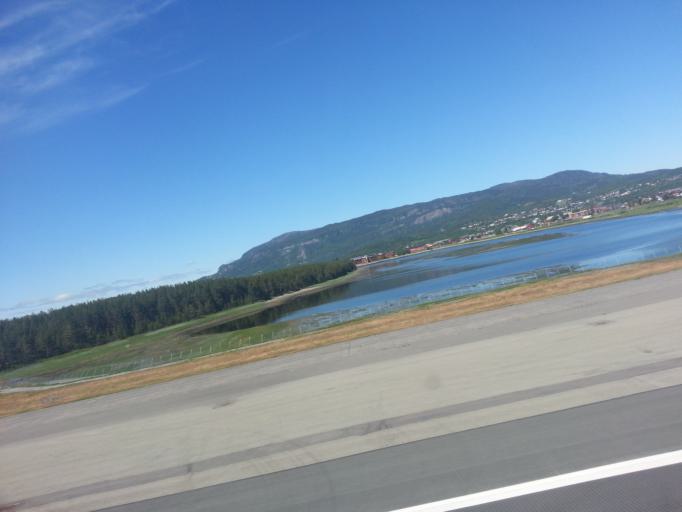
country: NO
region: Nord-Trondelag
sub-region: Stjordal
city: Stjordal
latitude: 63.4581
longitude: 10.9061
